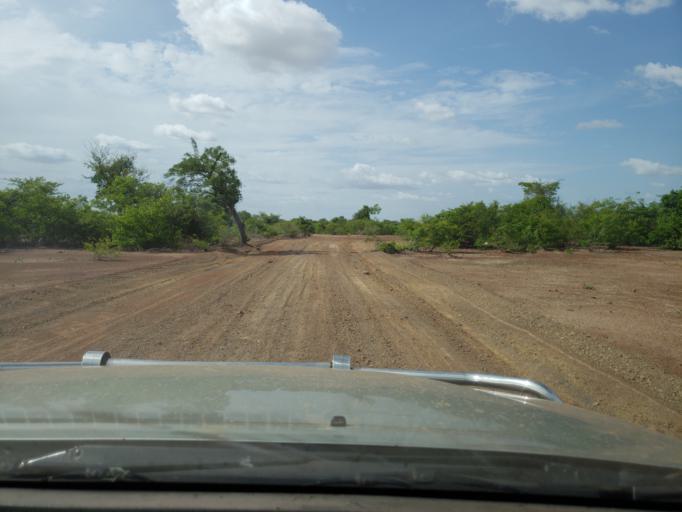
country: ML
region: Segou
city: Bla
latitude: 12.7821
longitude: -5.6084
